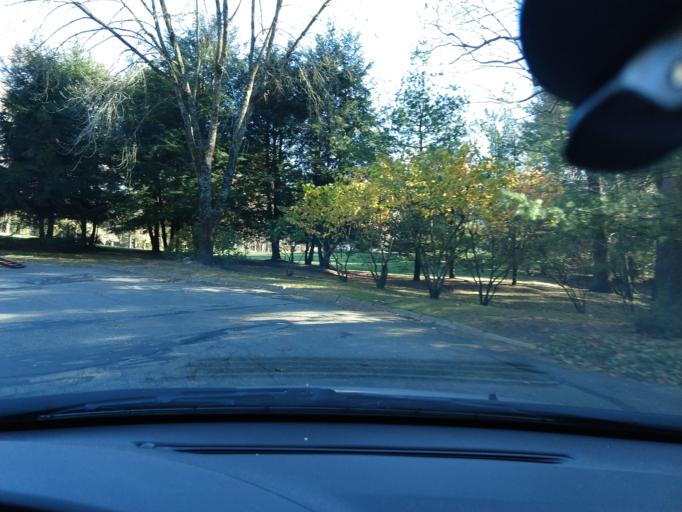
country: US
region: Massachusetts
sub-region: Middlesex County
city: Concord
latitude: 42.4849
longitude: -71.3328
